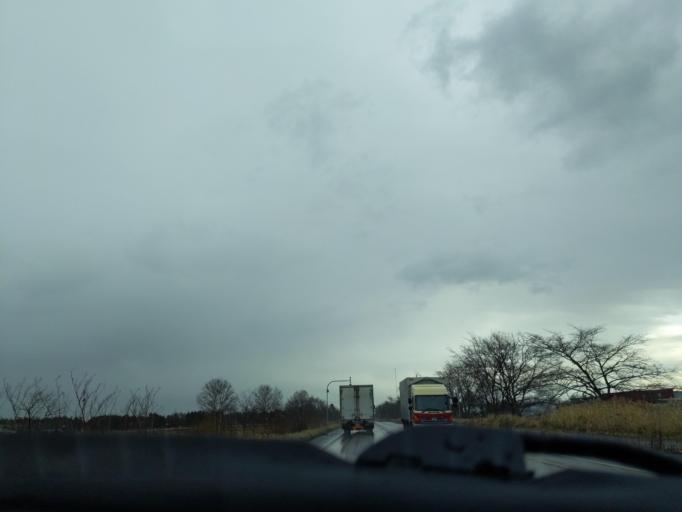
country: JP
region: Hokkaido
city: Ebetsu
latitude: 43.1097
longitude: 141.5920
